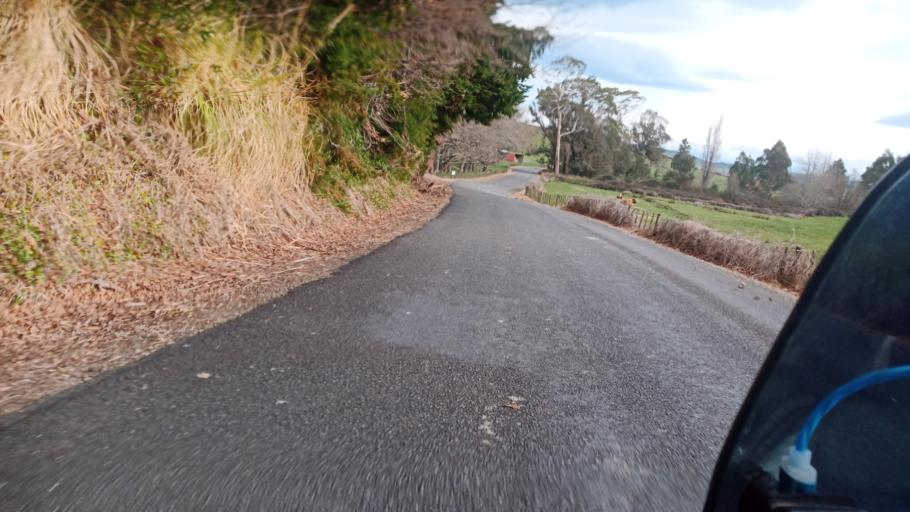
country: NZ
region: Hawke's Bay
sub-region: Wairoa District
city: Wairoa
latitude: -38.9749
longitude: 177.4262
